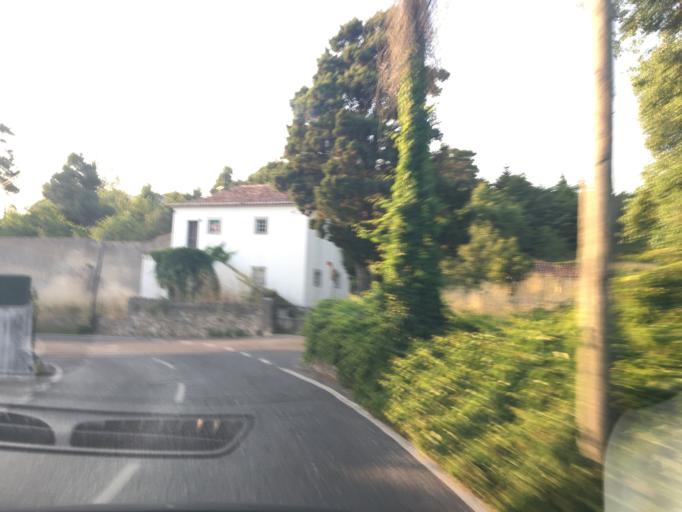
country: PT
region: Lisbon
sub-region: Sintra
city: Sintra
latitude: 38.8089
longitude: -9.3873
